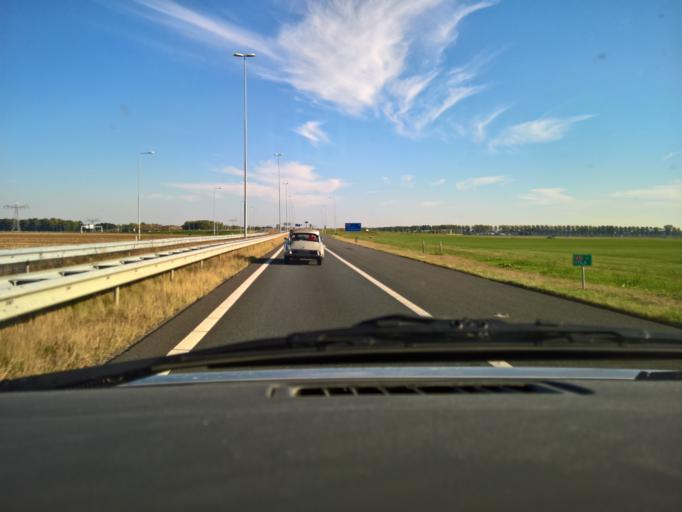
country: NL
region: Gelderland
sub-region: Gemeente Wijchen
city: Bergharen
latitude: 51.8608
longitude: 5.7036
